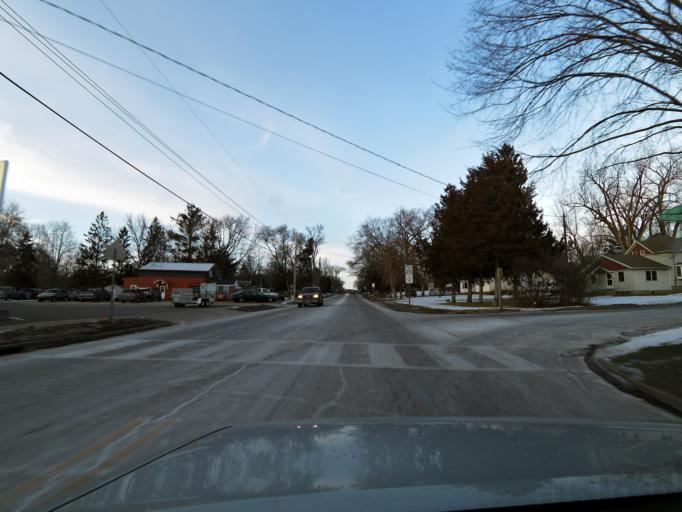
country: US
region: Wisconsin
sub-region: Saint Croix County
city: North Hudson
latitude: 44.9973
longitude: -92.7565
